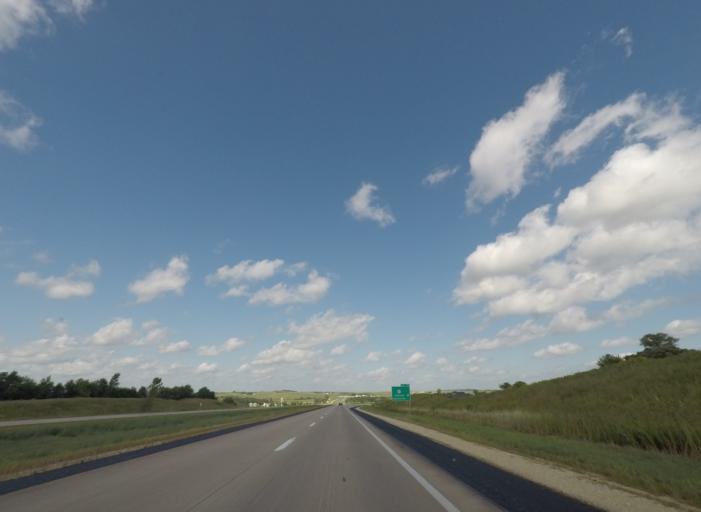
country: US
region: Iowa
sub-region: Dubuque County
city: Cascade
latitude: 42.2993
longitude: -91.0305
